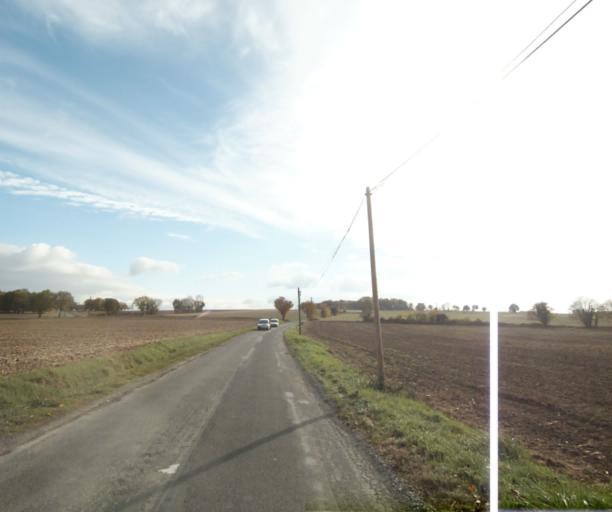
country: FR
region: Poitou-Charentes
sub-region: Departement de la Charente-Maritime
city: Saint-Georges-des-Coteaux
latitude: 45.7588
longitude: -0.7118
